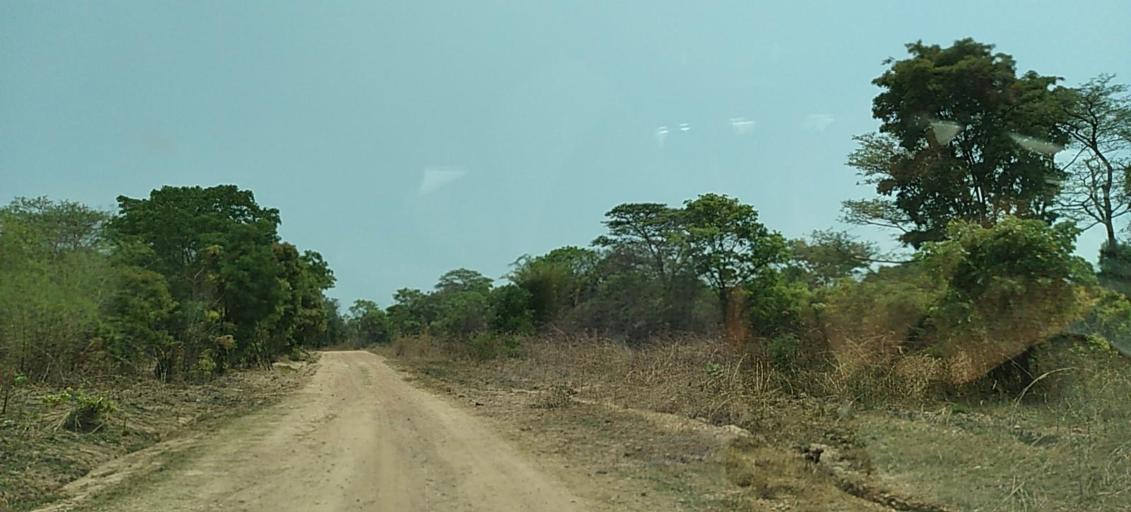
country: ZM
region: Copperbelt
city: Kalulushi
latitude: -12.9542
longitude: 28.1500
